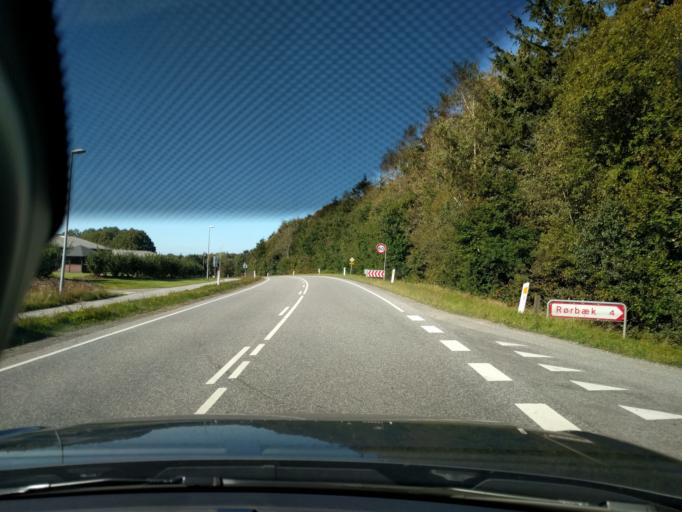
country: DK
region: North Denmark
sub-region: Vesthimmerland Kommune
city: Alestrup
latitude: 56.7021
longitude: 9.6433
